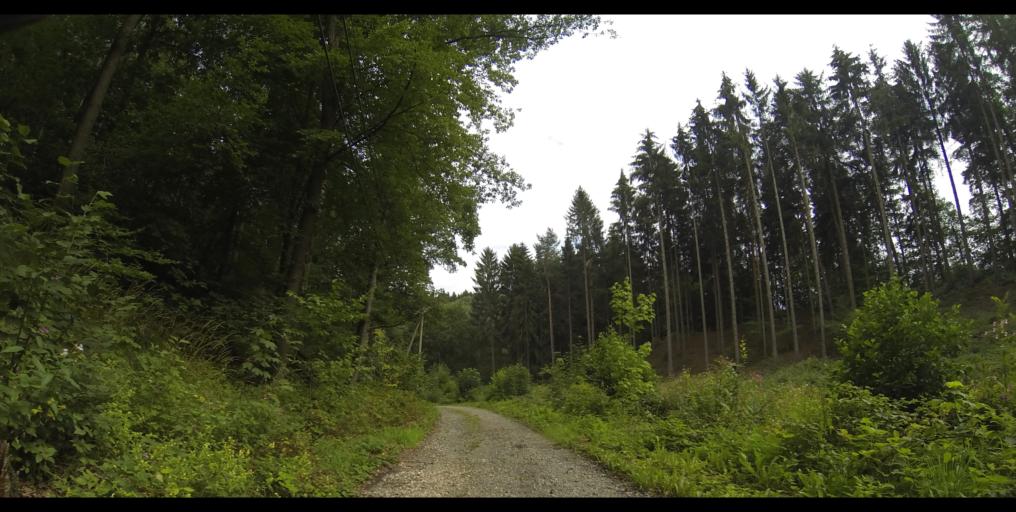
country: DE
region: Saxony
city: Grossschirma
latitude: 51.0034
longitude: 13.3112
